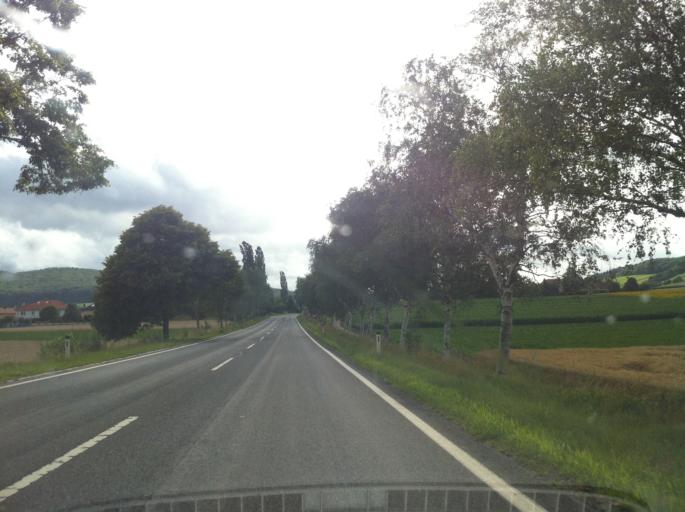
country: AT
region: Lower Austria
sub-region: Politischer Bezirk Tulln
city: Sieghartskirchen
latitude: 48.2539
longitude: 16.0578
